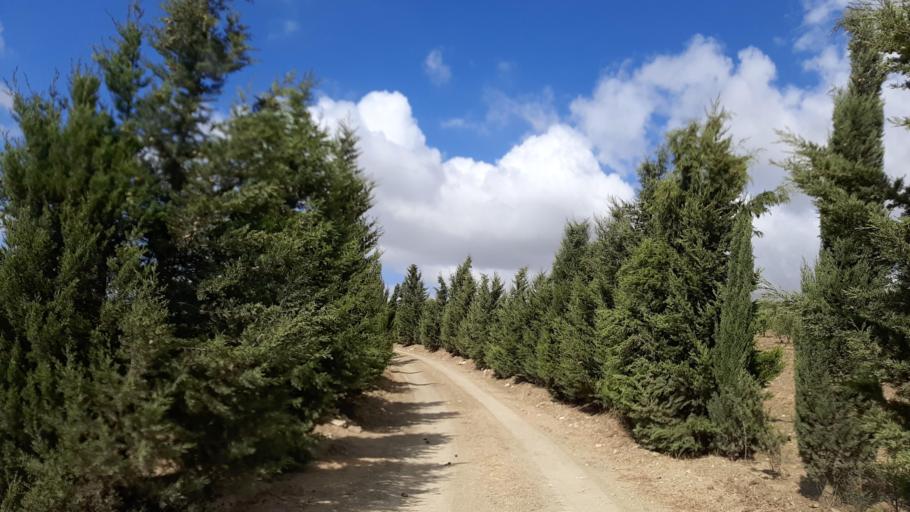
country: TN
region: Zaghwan
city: Zaghouan
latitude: 36.5025
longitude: 10.1830
